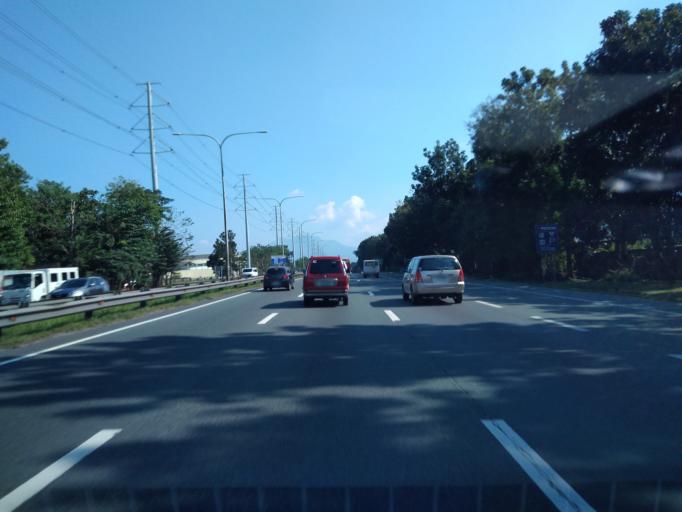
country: PH
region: Calabarzon
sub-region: Province of Laguna
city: Cabuyao
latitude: 14.2404
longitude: 121.1120
